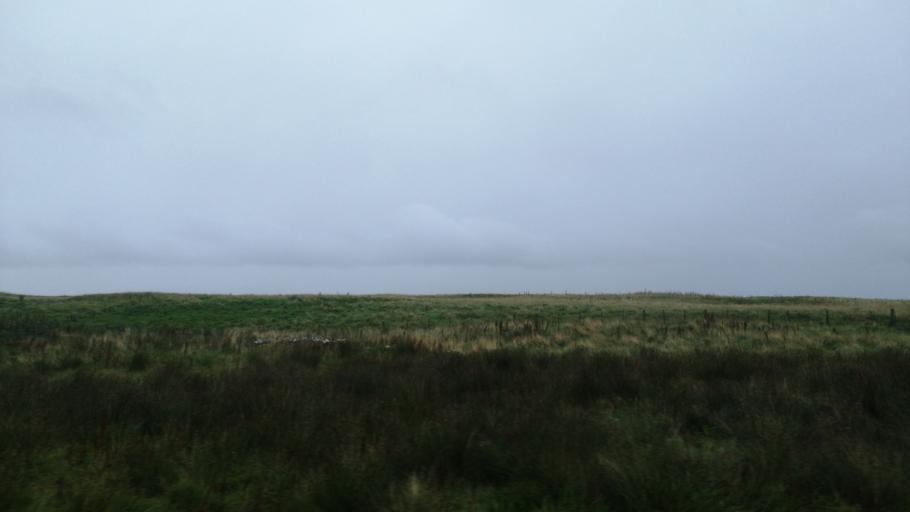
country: GB
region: Scotland
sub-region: Highland
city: Brora
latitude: 58.0322
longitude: -3.8430
